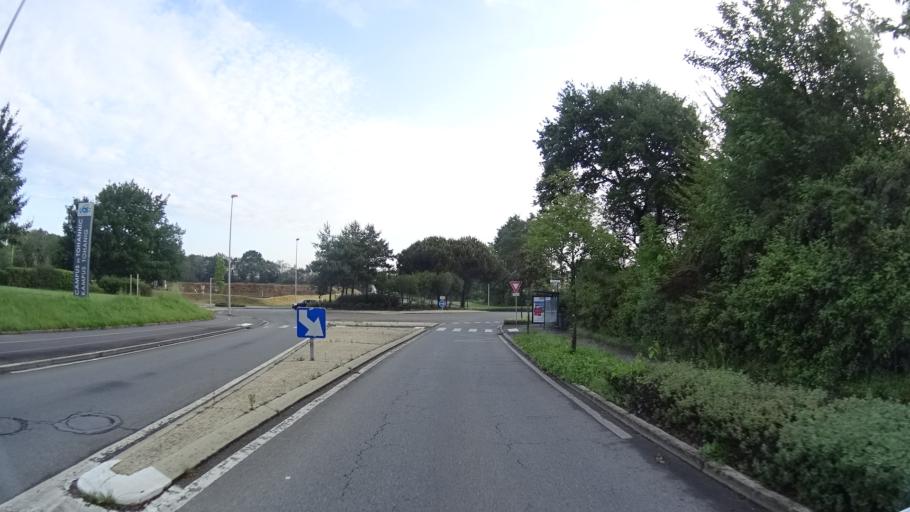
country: FR
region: Brittany
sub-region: Departement du Morbihan
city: Vannes
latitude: 47.6461
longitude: -2.7436
